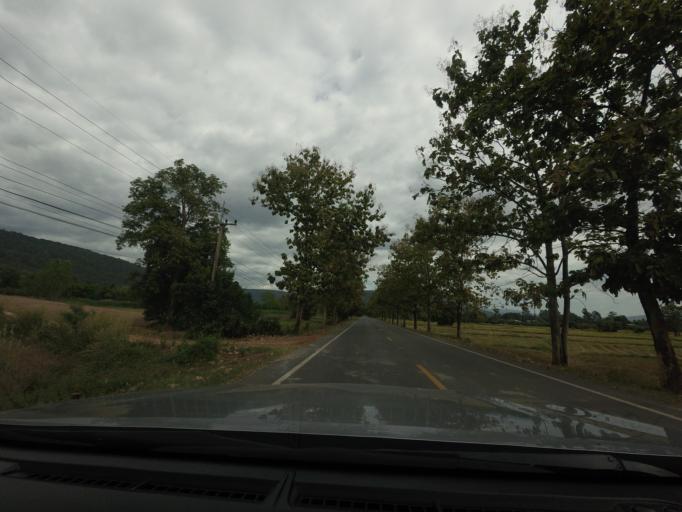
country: TH
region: Phitsanulok
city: Noen Maprang
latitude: 16.7015
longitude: 100.5656
